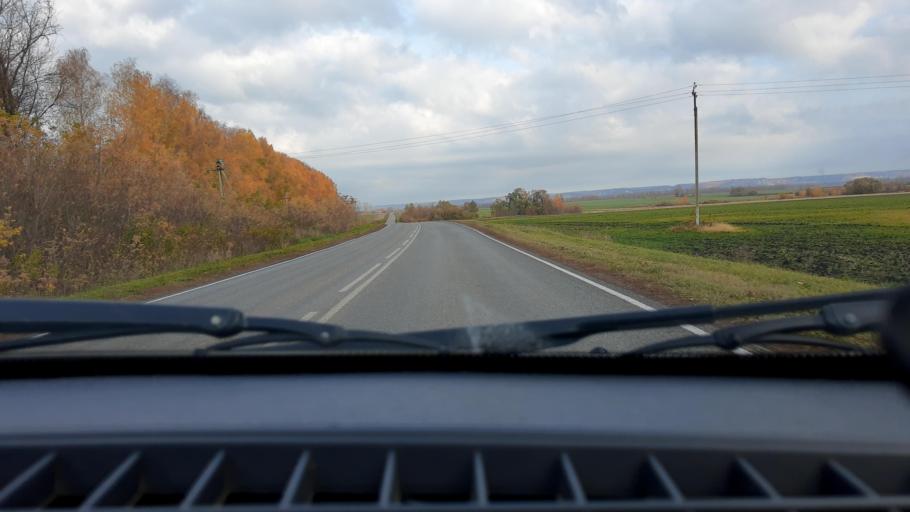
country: RU
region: Bashkortostan
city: Ulukulevo
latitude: 54.3971
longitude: 56.3793
